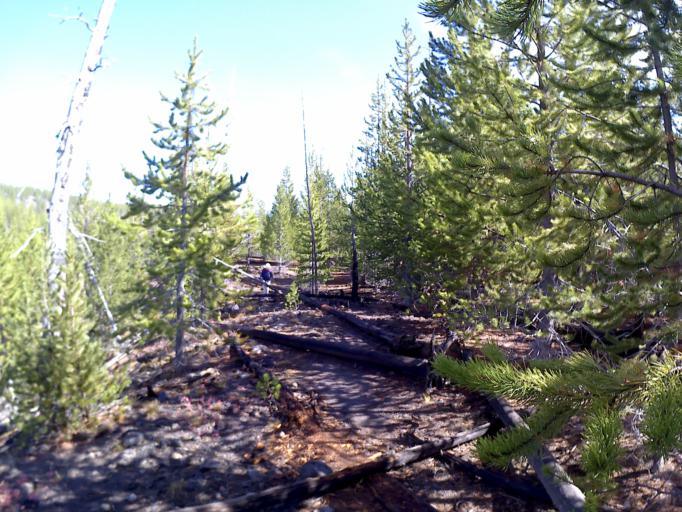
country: US
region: Montana
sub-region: Gallatin County
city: West Yellowstone
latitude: 44.4881
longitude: -110.8675
